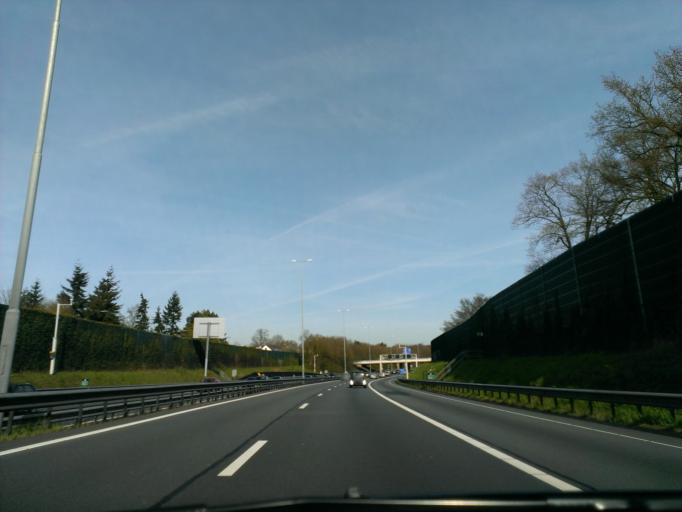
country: NL
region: North Holland
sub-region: Gemeente Bussum
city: Bussum
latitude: 52.2761
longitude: 5.1876
